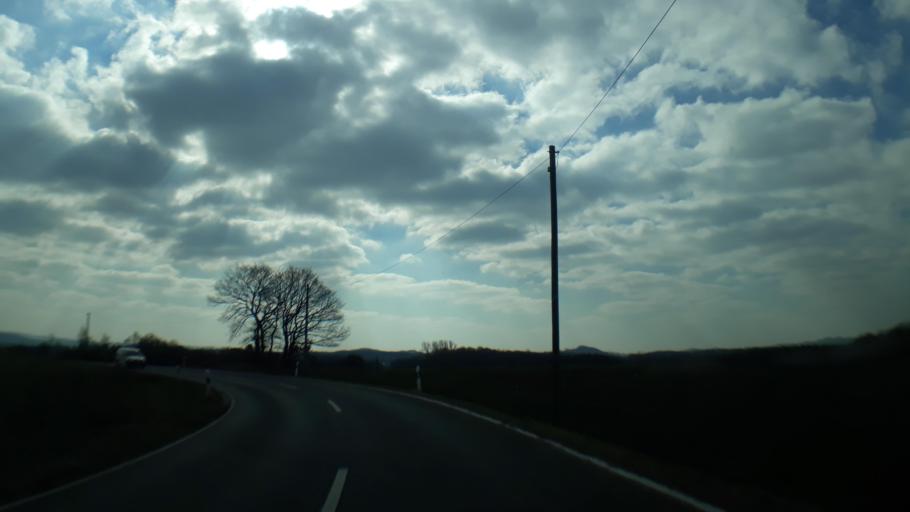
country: DE
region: Rheinland-Pfalz
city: Berg
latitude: 50.5697
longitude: 6.9460
